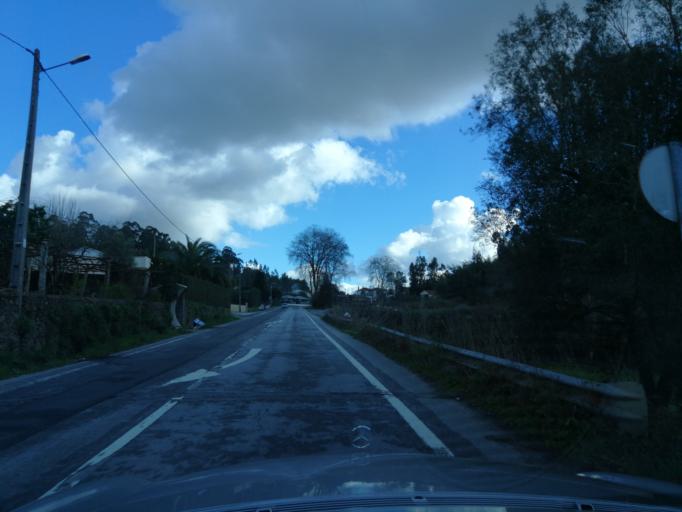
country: PT
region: Viana do Castelo
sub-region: Ponte de Lima
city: Ponte de Lima
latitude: 41.7071
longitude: -8.5393
